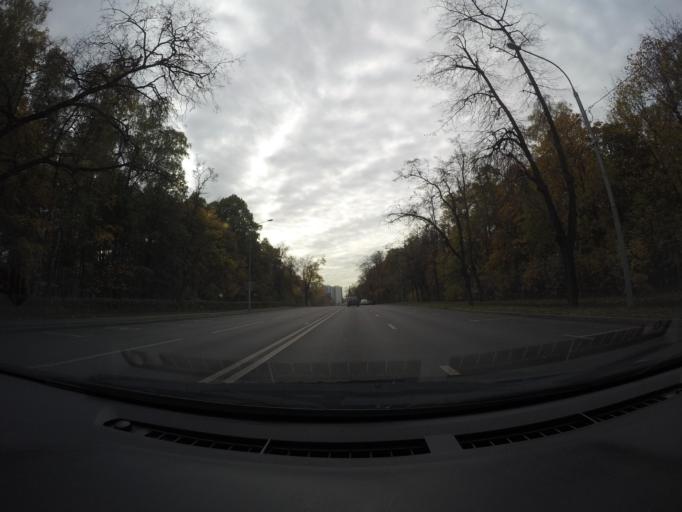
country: RU
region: Moscow
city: Sokol'niki
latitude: 55.7956
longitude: 37.6821
